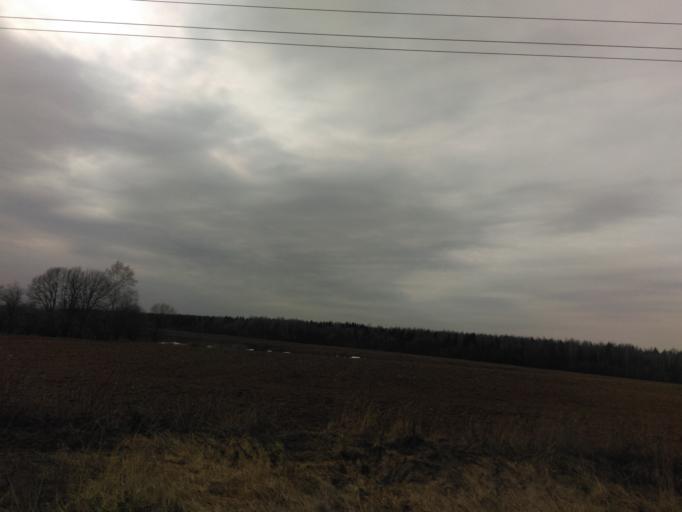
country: RU
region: Moskovskaya
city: Zvenigorod
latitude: 55.7494
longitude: 36.9363
